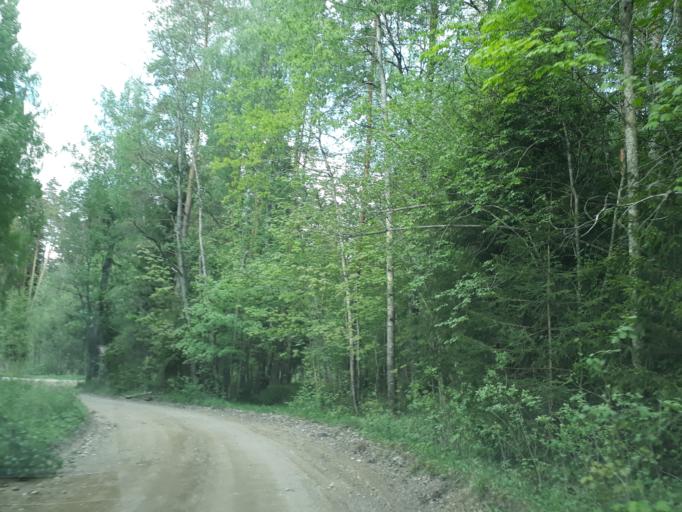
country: LV
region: Ligatne
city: Ligatne
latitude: 57.2745
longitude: 24.9910
